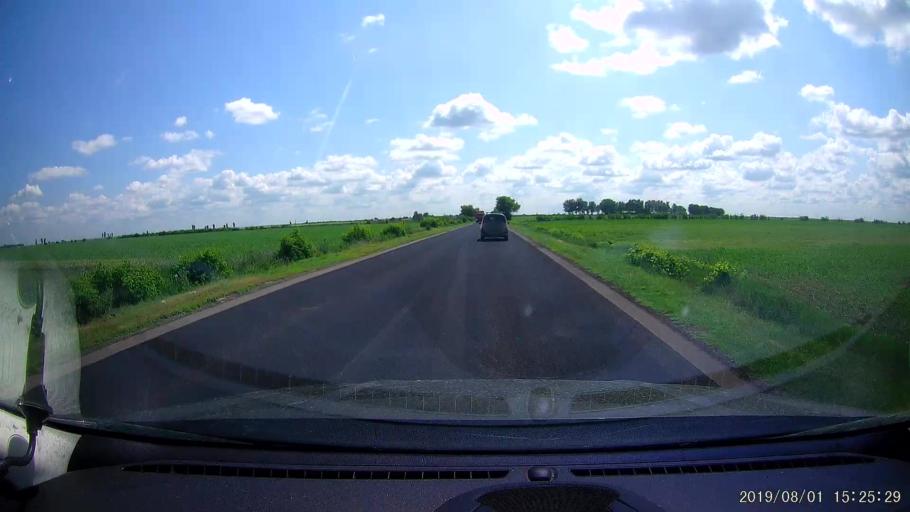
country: RO
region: Braila
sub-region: Comuna Viziru
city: Lanurile
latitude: 45.0215
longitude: 27.7348
